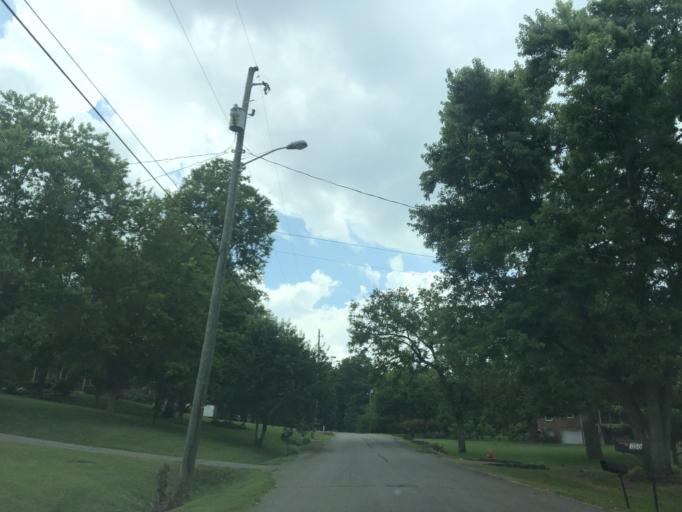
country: US
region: Tennessee
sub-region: Davidson County
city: Lakewood
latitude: 36.1648
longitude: -86.6707
